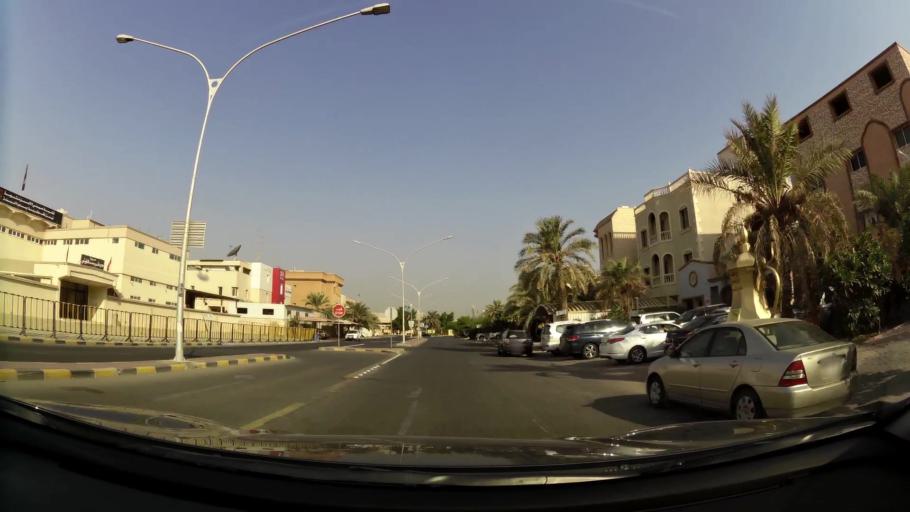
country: KW
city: Bayan
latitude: 29.3175
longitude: 48.0439
